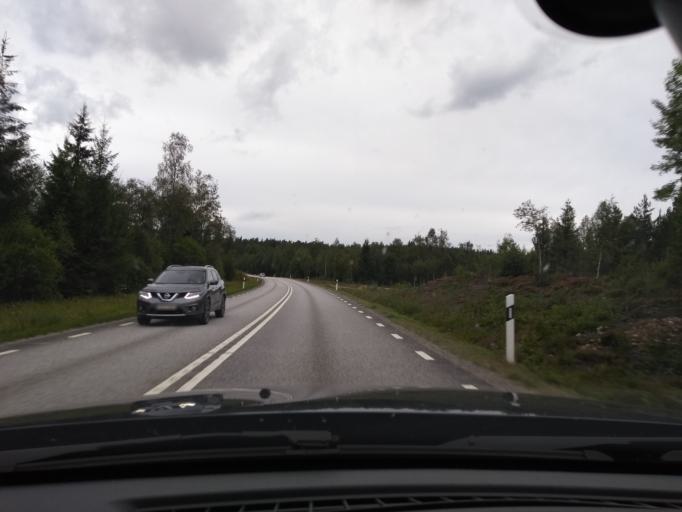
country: SE
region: OEstergoetland
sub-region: Ydre Kommun
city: OEsterbymo
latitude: 57.6434
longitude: 15.2099
